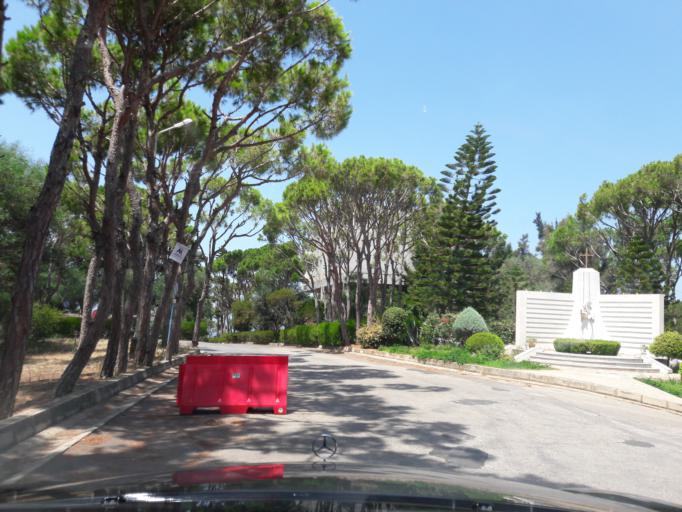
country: LB
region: Mont-Liban
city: Djounie
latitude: 33.9349
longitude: 35.6192
